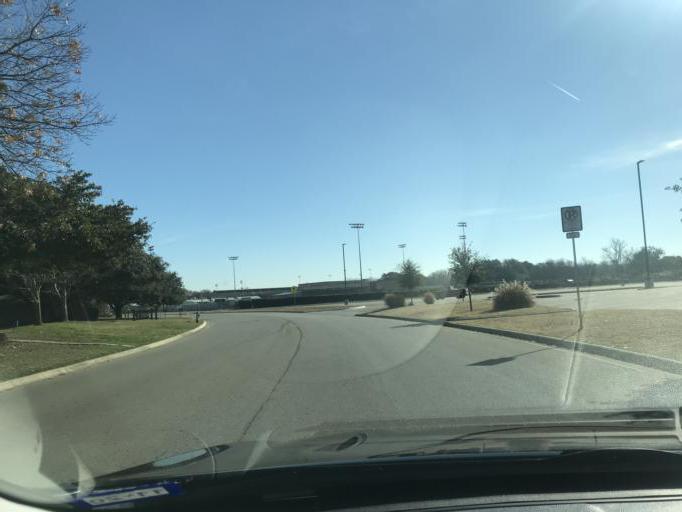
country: US
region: Texas
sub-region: Denton County
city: Denton
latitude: 33.2262
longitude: -97.1486
